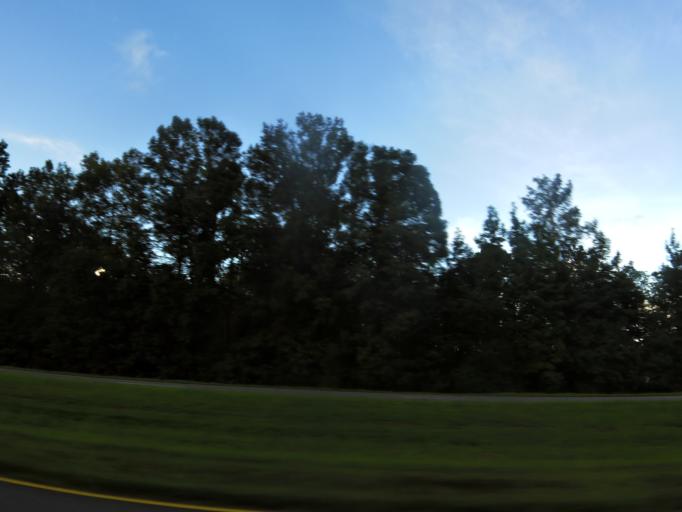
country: US
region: Georgia
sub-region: Camden County
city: St Marys
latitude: 30.7568
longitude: -81.6208
